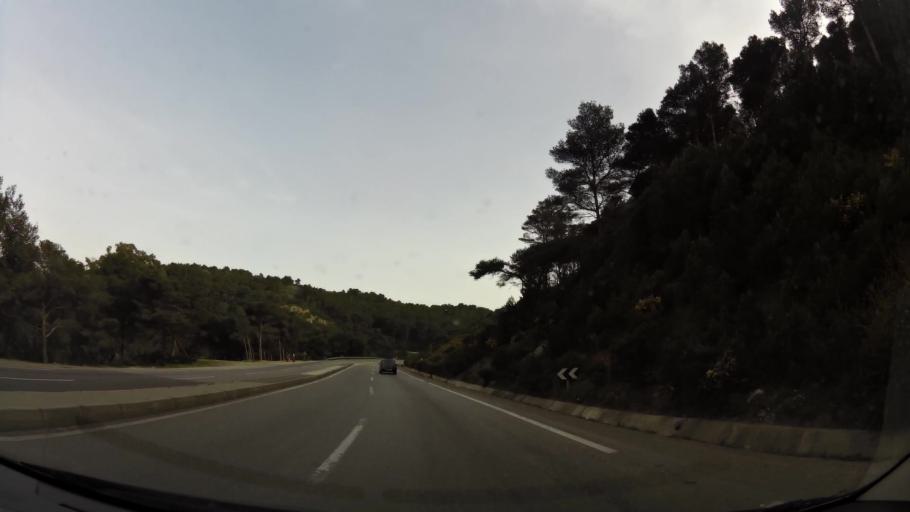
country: MA
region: Tanger-Tetouan
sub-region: Tanger-Assilah
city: Dar Chaoui
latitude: 35.5618
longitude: -5.5847
